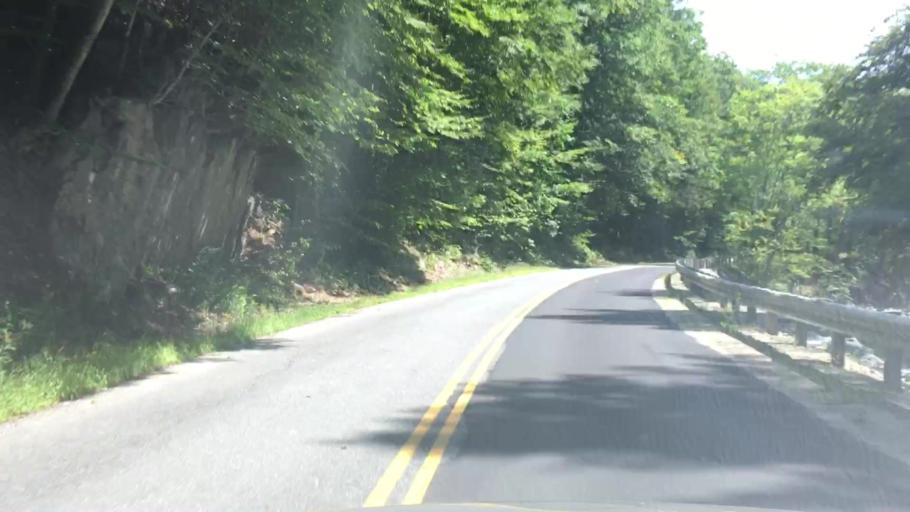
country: US
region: Vermont
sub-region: Windham County
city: West Brattleboro
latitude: 42.8044
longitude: -72.6989
